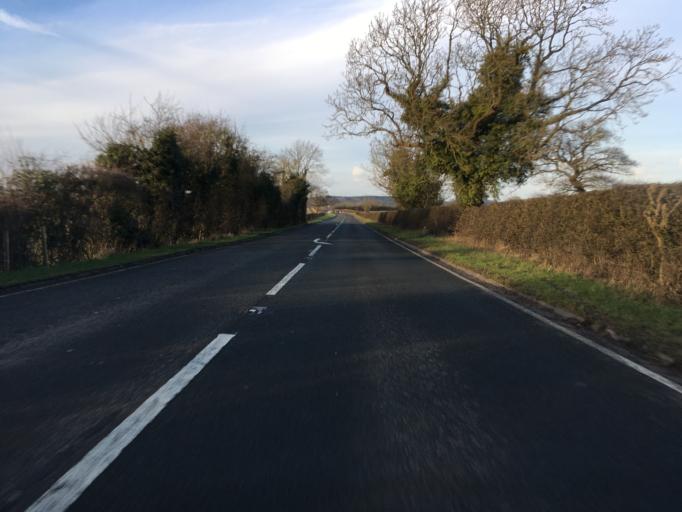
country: GB
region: England
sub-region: Warwickshire
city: Stratford-upon-Avon
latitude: 52.2325
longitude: -1.7414
